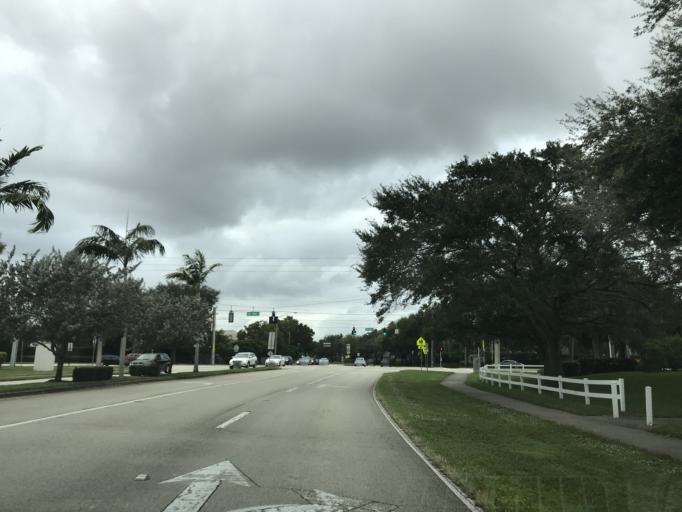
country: US
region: Florida
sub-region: Broward County
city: Coral Springs
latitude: 26.2983
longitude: -80.2674
